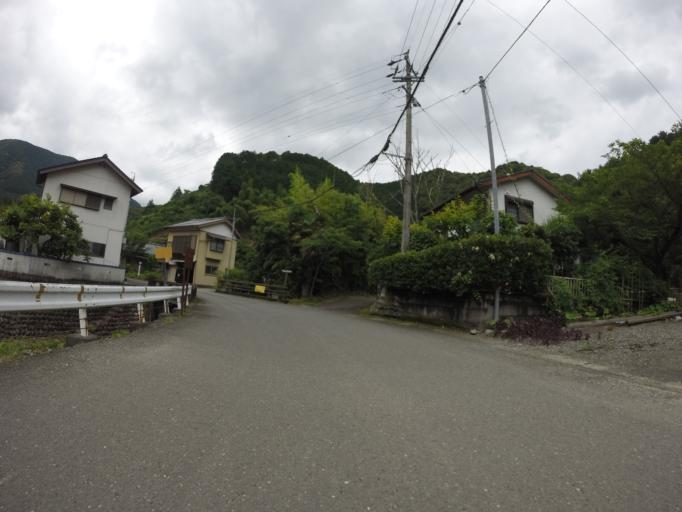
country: JP
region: Shizuoka
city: Shizuoka-shi
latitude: 35.0116
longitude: 138.3144
